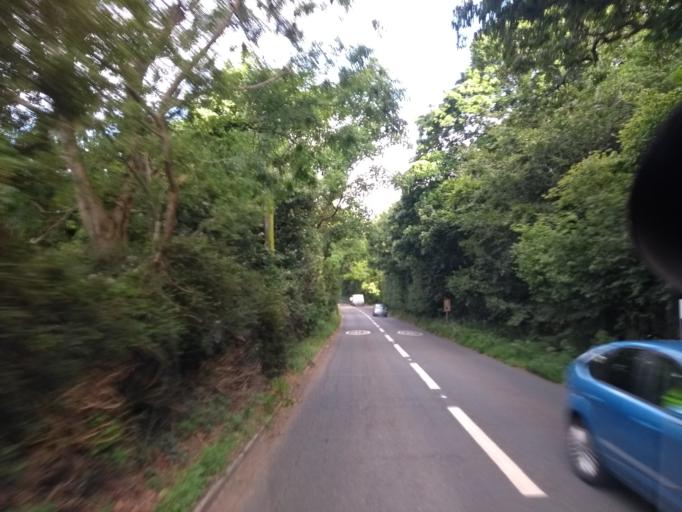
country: GB
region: England
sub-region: Somerset
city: Williton
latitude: 51.1689
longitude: -3.2780
